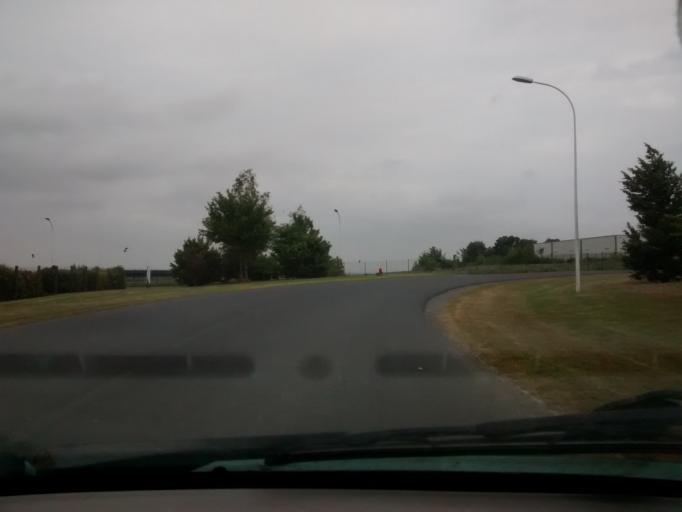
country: FR
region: Lower Normandy
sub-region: Departement de la Manche
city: Saint-Lo
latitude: 49.0971
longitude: -1.0716
